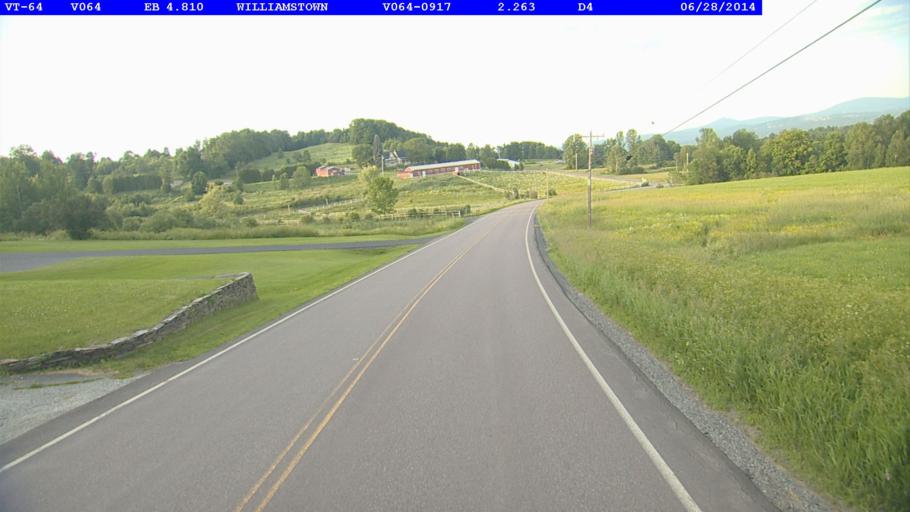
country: US
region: Vermont
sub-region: Orange County
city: Williamstown
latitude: 44.1159
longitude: -72.5744
